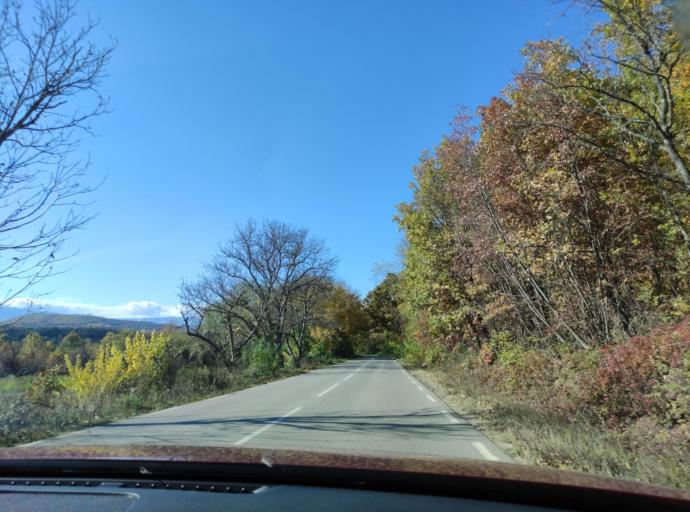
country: BG
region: Montana
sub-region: Obshtina Montana
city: Montana
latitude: 43.4072
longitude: 23.0624
